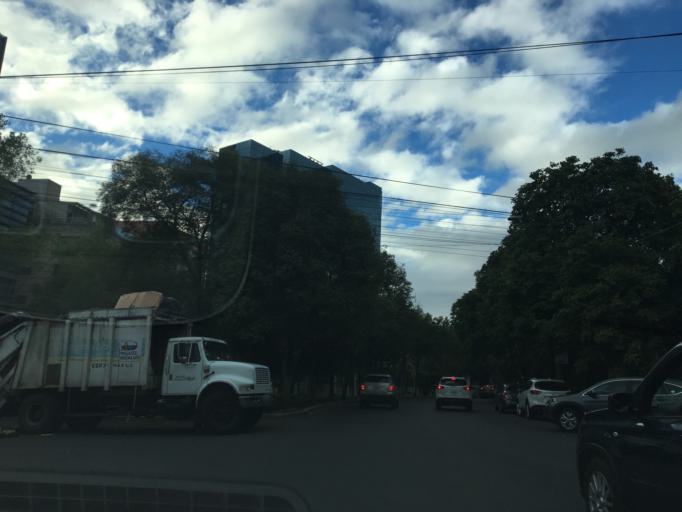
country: MX
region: Mexico City
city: Miguel Hidalgo
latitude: 19.4260
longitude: -99.2053
